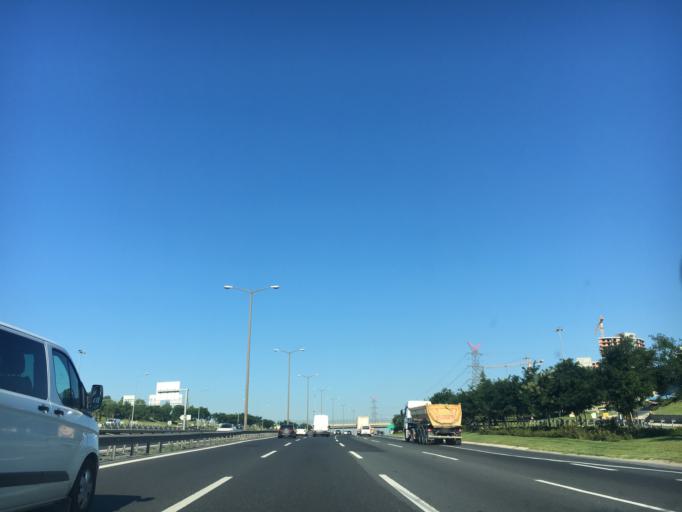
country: TR
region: Istanbul
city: Esenyurt
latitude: 41.0540
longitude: 28.6756
